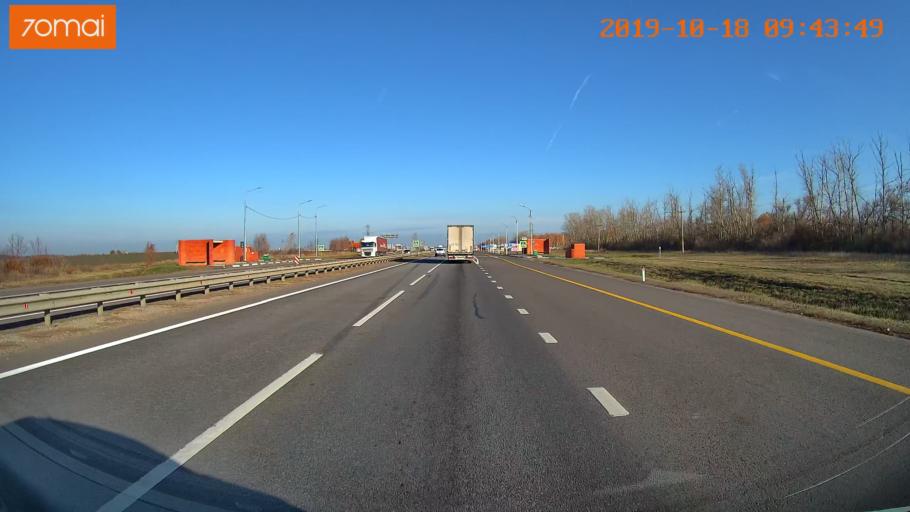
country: RU
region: Tula
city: Kazachka
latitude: 53.3034
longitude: 38.1786
